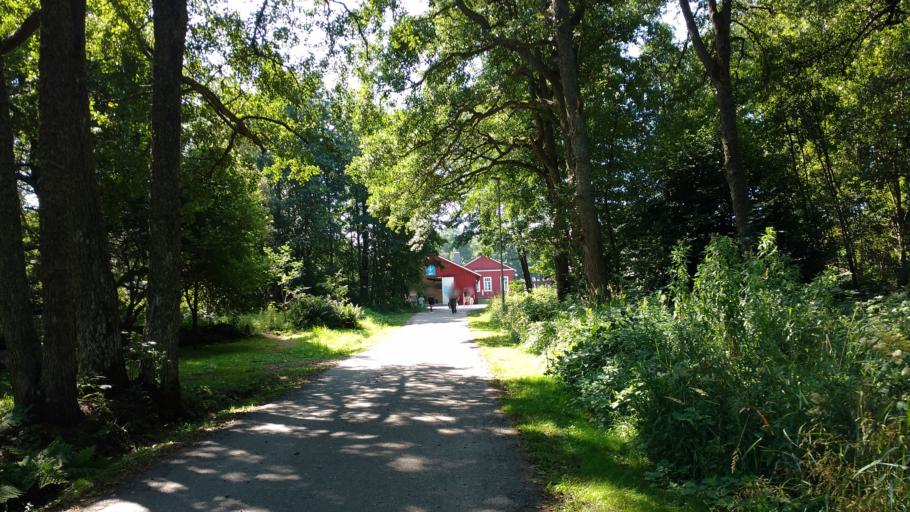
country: FI
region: Varsinais-Suomi
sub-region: Aboland-Turunmaa
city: Dragsfjaerd
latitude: 59.8081
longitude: 22.3379
